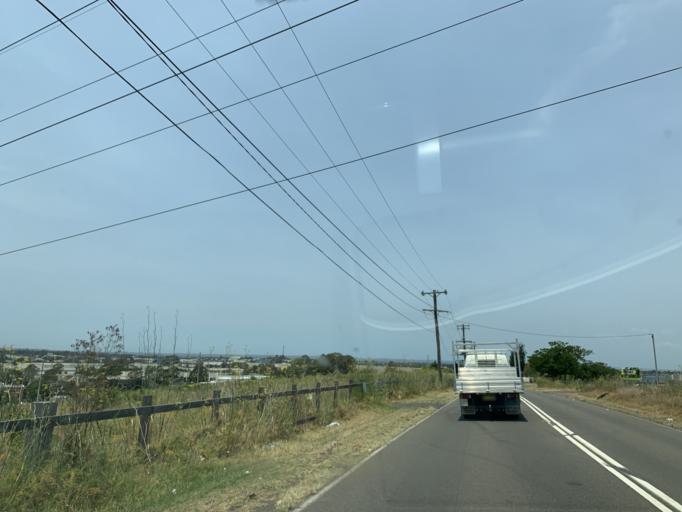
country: AU
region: New South Wales
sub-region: Fairfield
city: Horsley Park
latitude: -33.8359
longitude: 150.8794
